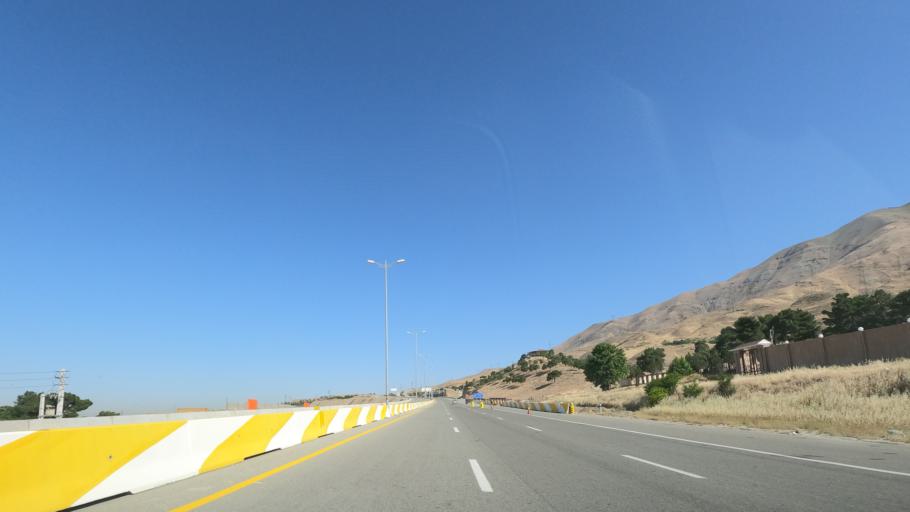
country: IR
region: Tehran
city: Shahr-e Qods
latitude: 35.7587
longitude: 51.0774
